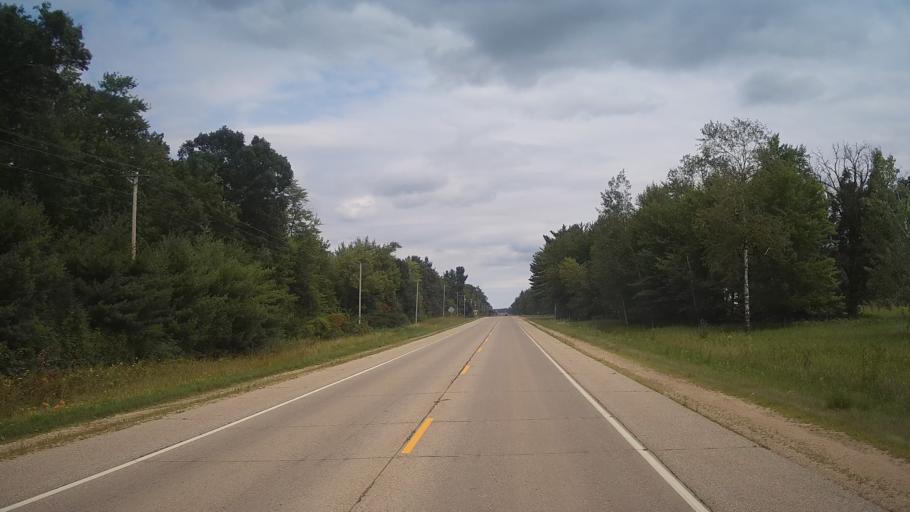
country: US
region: Wisconsin
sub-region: Waushara County
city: Redgranite
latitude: 44.0375
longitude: -89.0855
